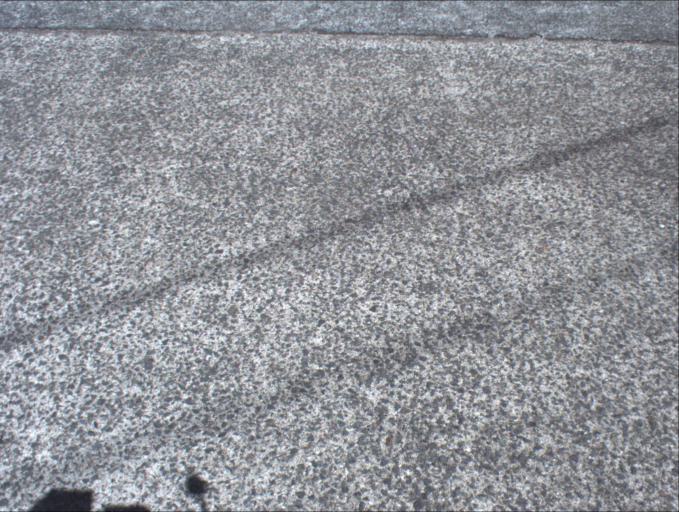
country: AU
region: Queensland
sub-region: Logan
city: Logan City
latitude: -27.6331
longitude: 153.1217
